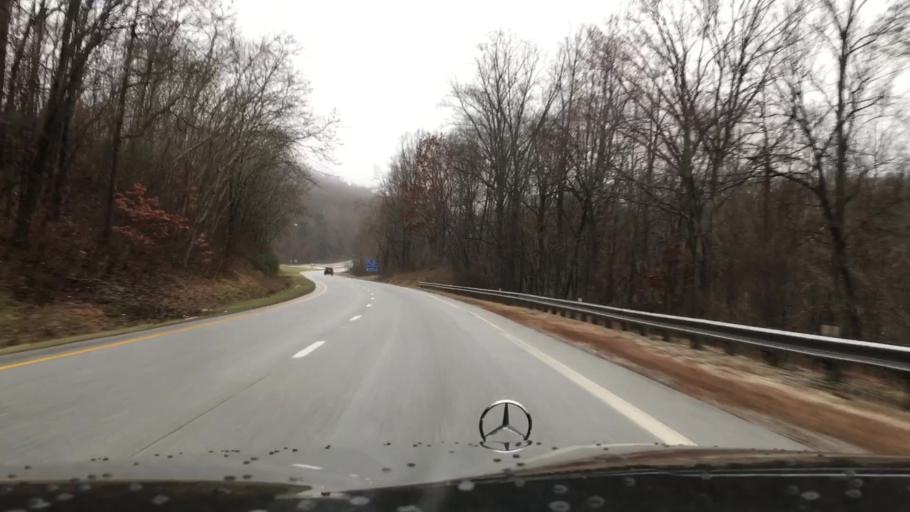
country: US
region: Virginia
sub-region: Nelson County
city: Nellysford
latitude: 37.8537
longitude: -78.7512
